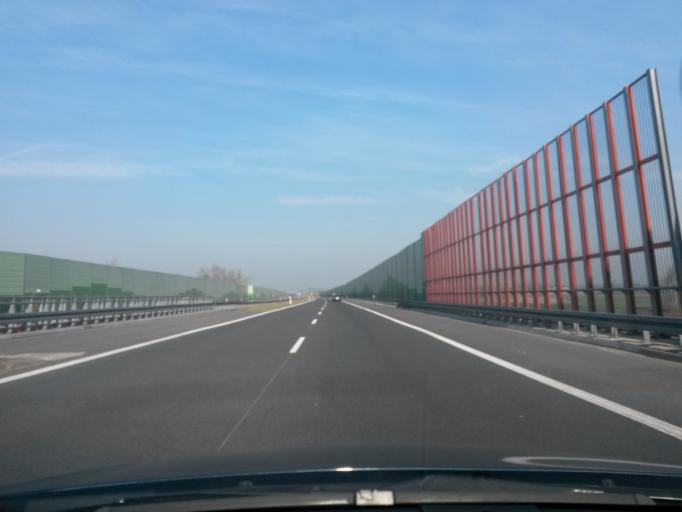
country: PL
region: Lodz Voivodeship
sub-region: Powiat leczycki
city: Piatek
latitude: 52.1157
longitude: 19.5046
